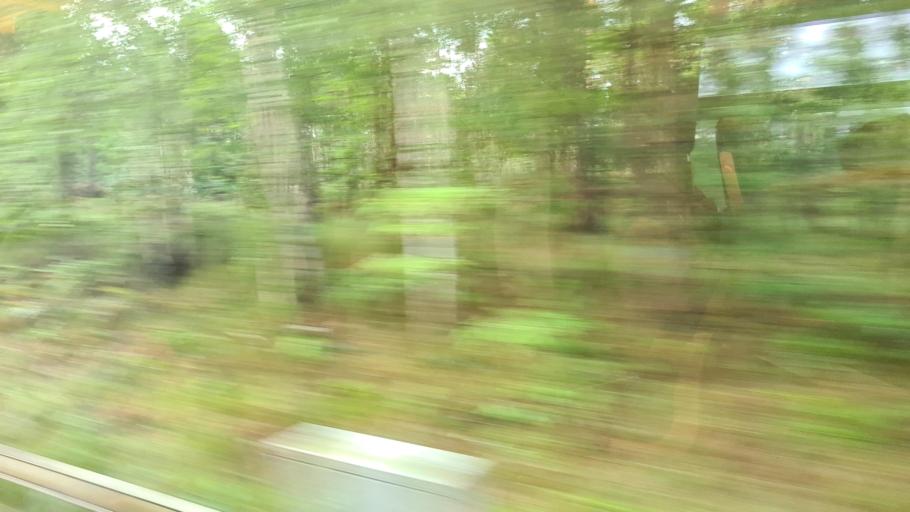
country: DE
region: Brandenburg
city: Schonewalde
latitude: 51.6295
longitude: 13.6222
